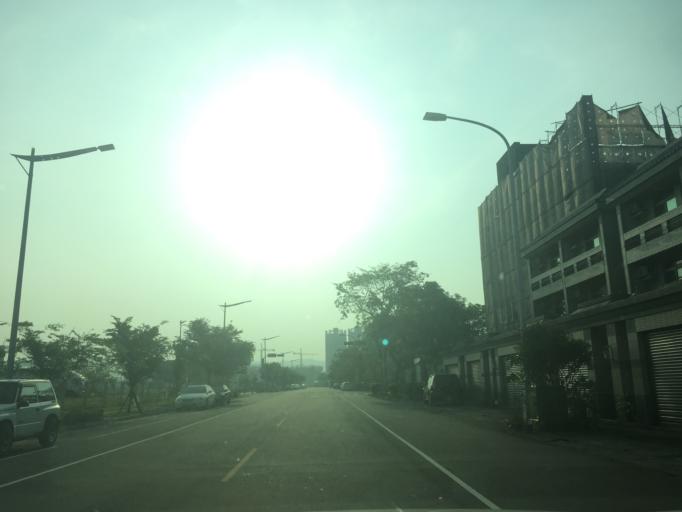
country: TW
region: Taiwan
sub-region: Taichung City
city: Taichung
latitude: 24.1967
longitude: 120.6772
